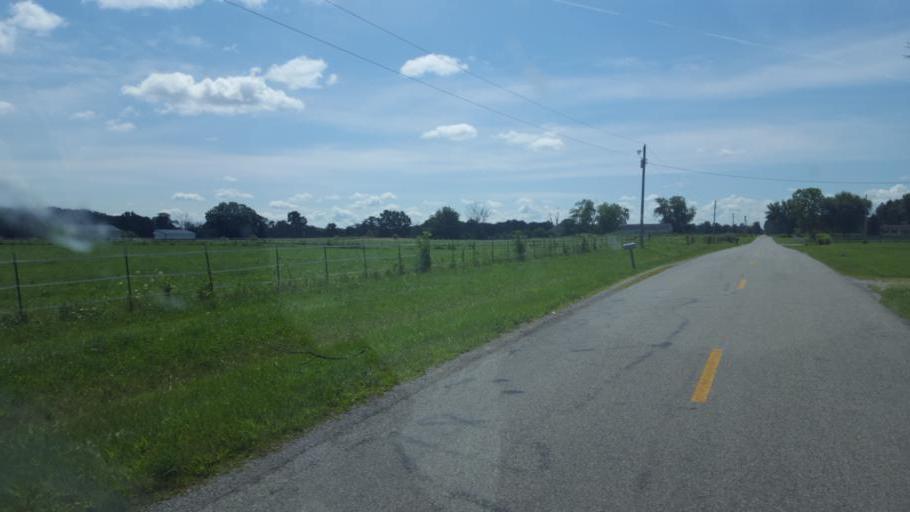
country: US
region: Ohio
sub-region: Delaware County
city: Sunbury
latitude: 40.3131
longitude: -82.7958
